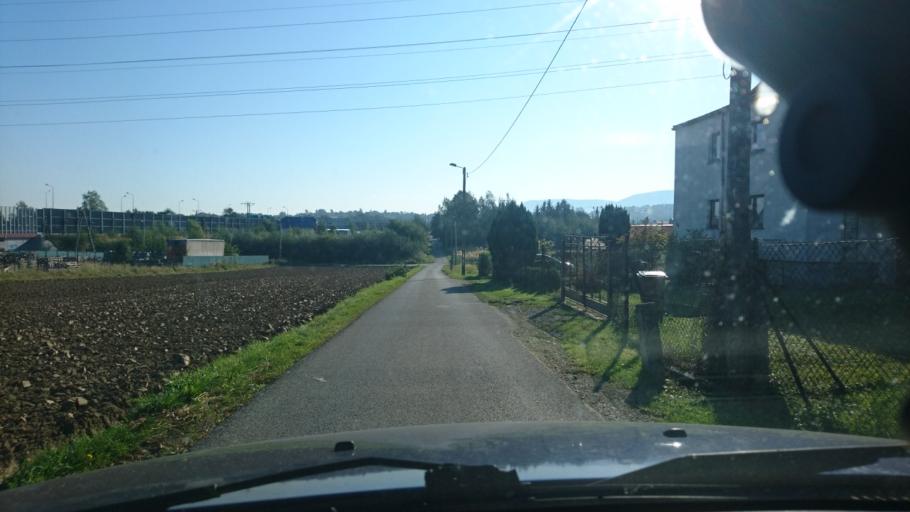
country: PL
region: Silesian Voivodeship
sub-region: Bielsko-Biala
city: Bielsko-Biala
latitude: 49.8462
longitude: 19.0600
